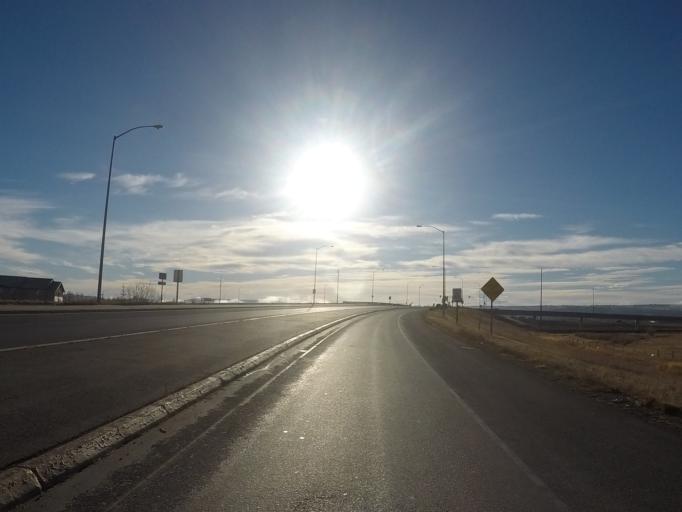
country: US
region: Montana
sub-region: Yellowstone County
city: Billings
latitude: 45.7344
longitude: -108.6069
